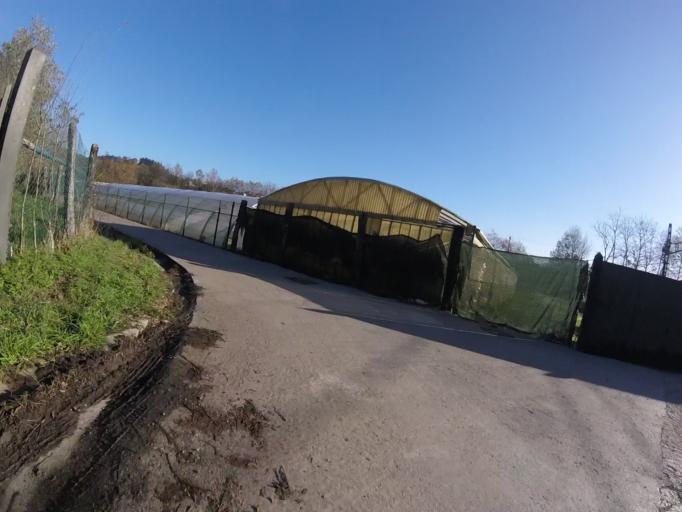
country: ES
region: Basque Country
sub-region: Provincia de Guipuzcoa
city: Usurbil
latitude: 43.2694
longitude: -2.0574
